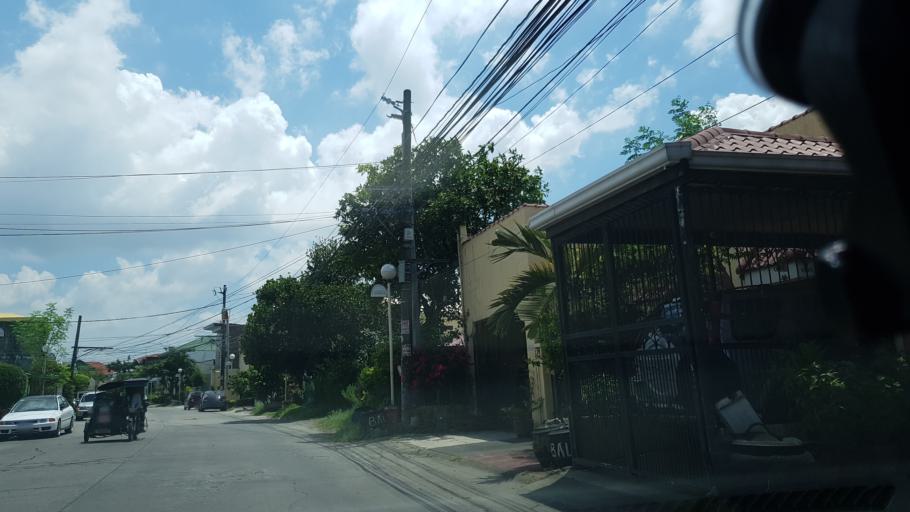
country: PH
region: Calabarzon
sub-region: Province of Rizal
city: Las Pinas
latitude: 14.4365
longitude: 120.9793
